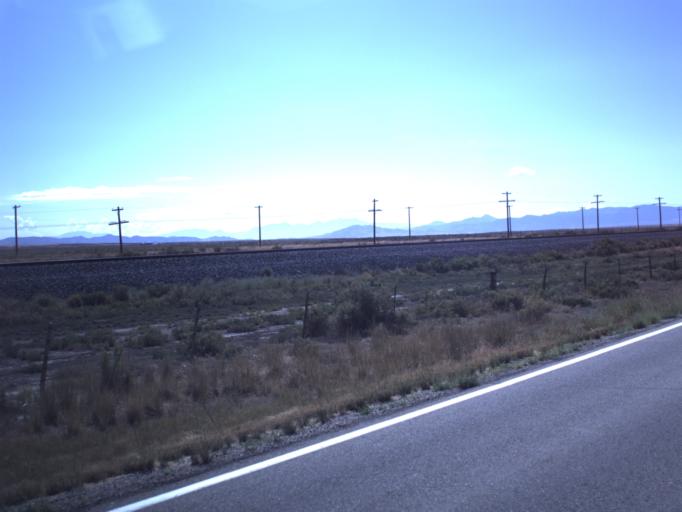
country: US
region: Utah
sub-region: Tooele County
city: Tooele
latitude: 40.3067
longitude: -112.4037
